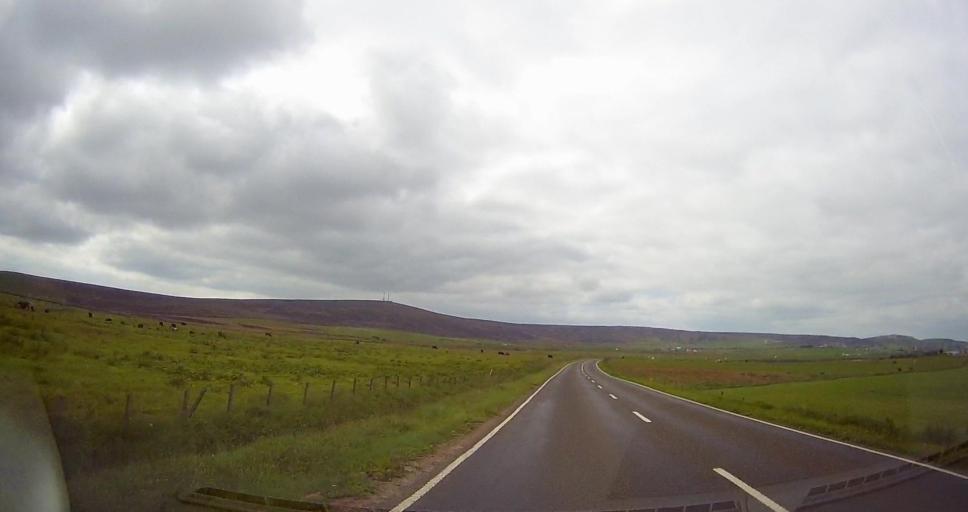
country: GB
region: Scotland
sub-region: Orkney Islands
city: Orkney
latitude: 58.9957
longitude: -3.0416
